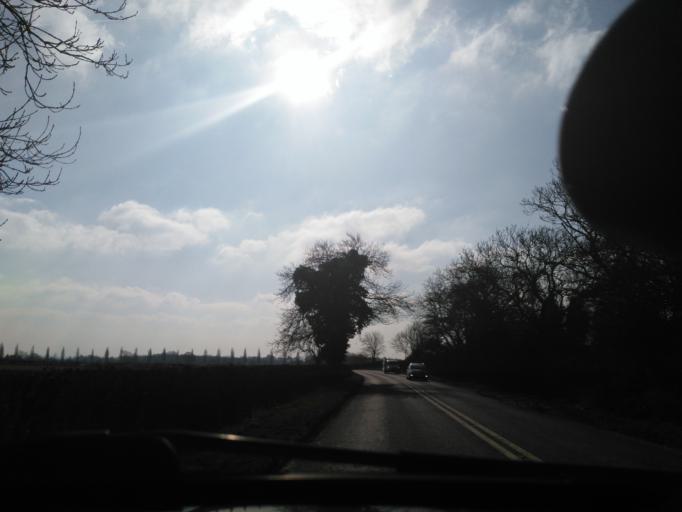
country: GB
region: England
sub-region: Wiltshire
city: Charlton
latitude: 51.6239
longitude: -2.0755
